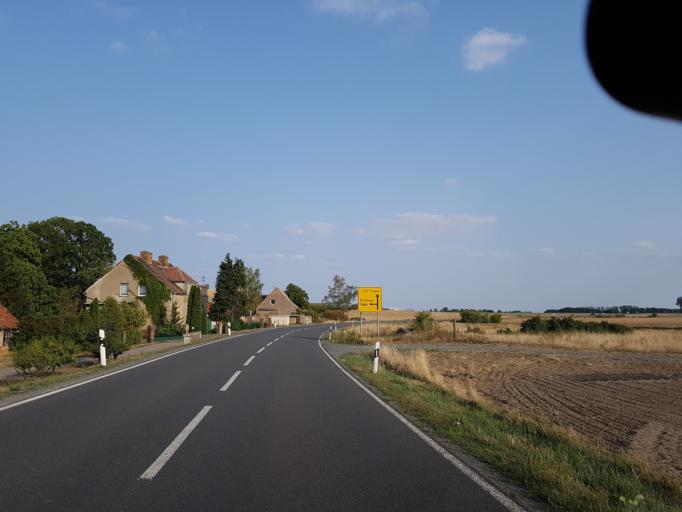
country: DE
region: Saxony
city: Dommitzsch
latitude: 51.6308
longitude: 12.8987
